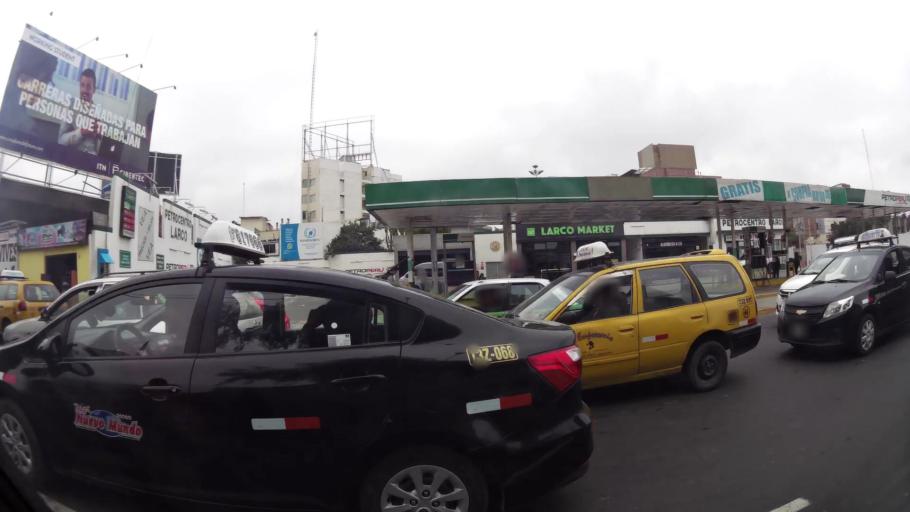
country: PE
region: La Libertad
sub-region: Provincia de Trujillo
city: Trujillo
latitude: -8.1161
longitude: -79.0315
